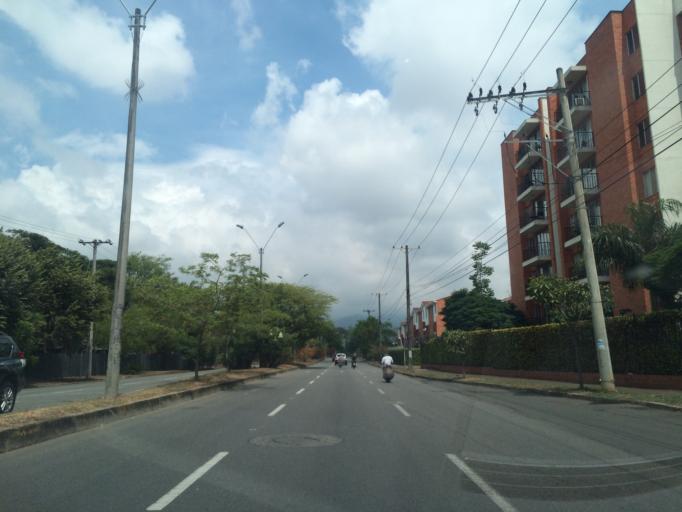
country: CO
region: Valle del Cauca
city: Cali
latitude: 3.3928
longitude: -76.5284
